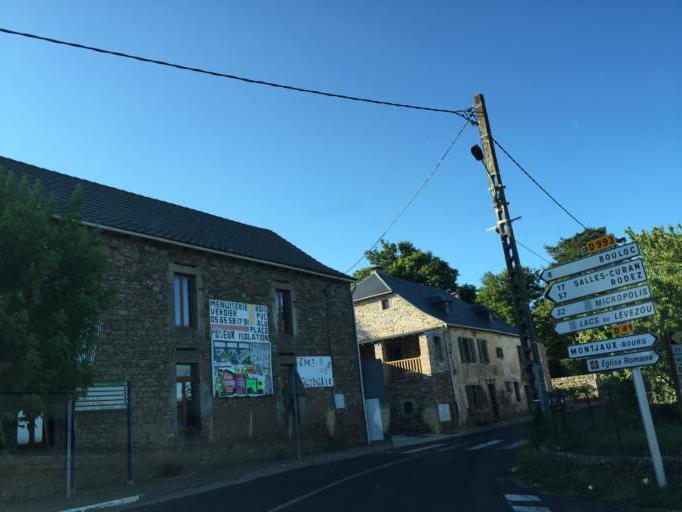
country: FR
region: Midi-Pyrenees
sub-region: Departement de l'Aveyron
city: Saint-Georges-de-Luzencon
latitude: 44.1006
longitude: 2.8989
